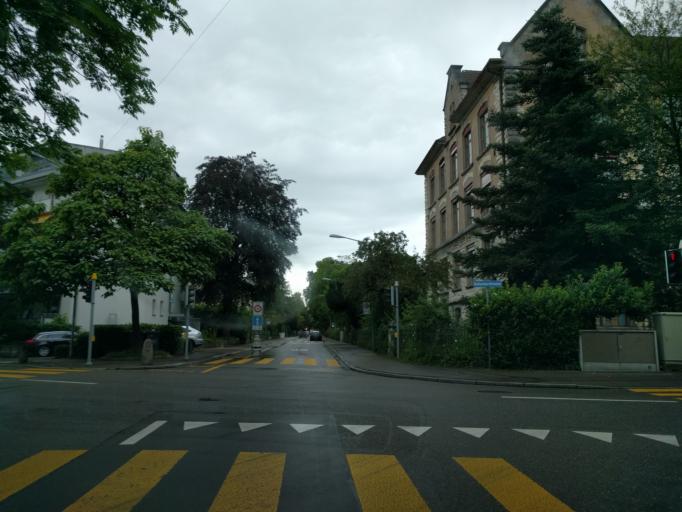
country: CH
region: Zurich
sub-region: Bezirk Zuerich
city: Zuerich (Kreis 7) / Hirslanden
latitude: 47.3615
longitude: 8.5654
